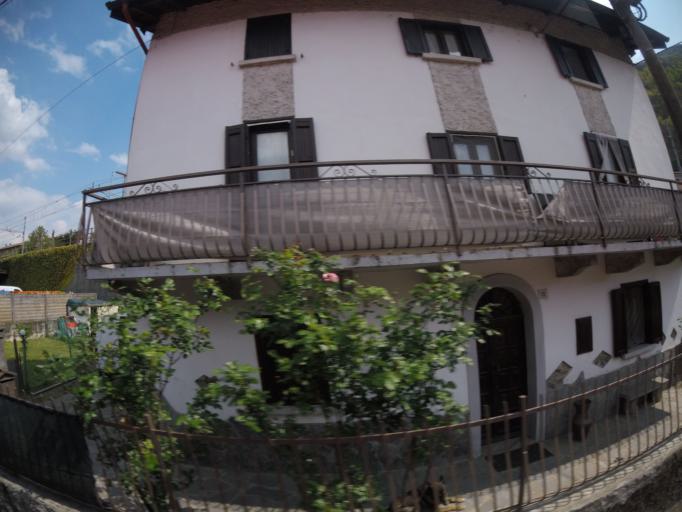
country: IT
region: Piedmont
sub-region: Provincia Verbano-Cusio-Ossola
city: Omegna
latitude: 45.8676
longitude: 8.4135
